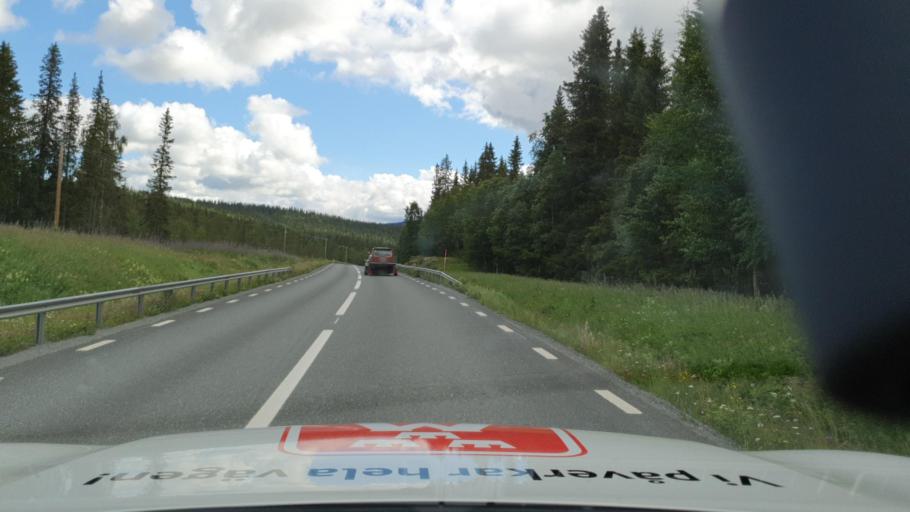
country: SE
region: Vaesterbotten
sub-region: Vilhelmina Kommun
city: Sjoberg
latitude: 65.5024
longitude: 15.7269
